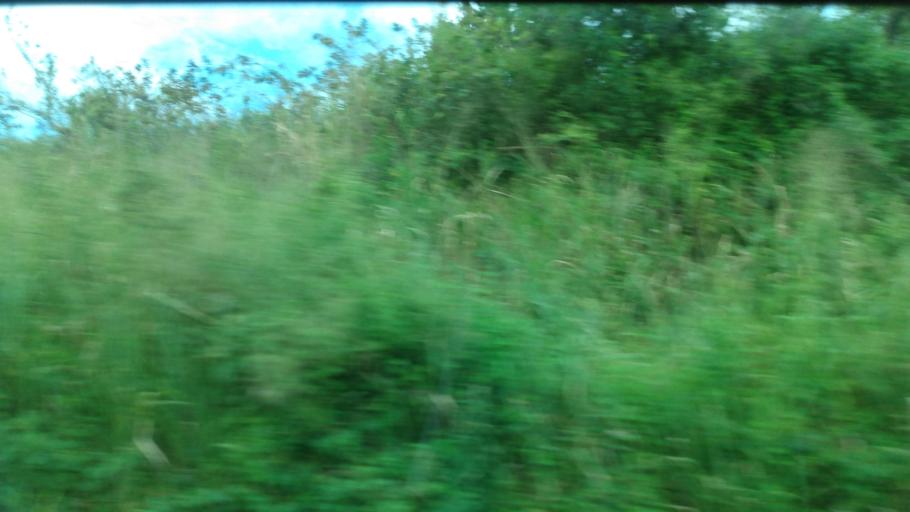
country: BR
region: Pernambuco
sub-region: Maraial
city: Maraial
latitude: -8.7251
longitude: -35.7908
